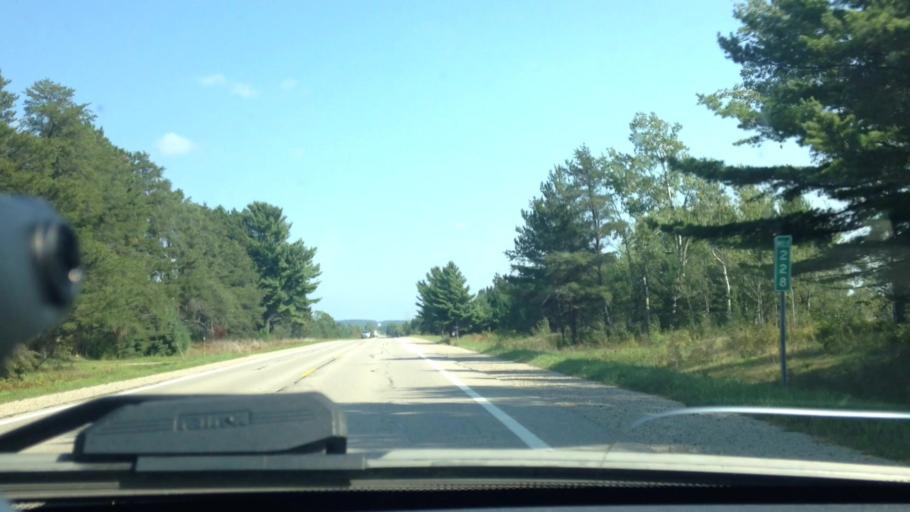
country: US
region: Michigan
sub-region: Luce County
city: Newberry
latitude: 46.3102
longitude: -85.6338
